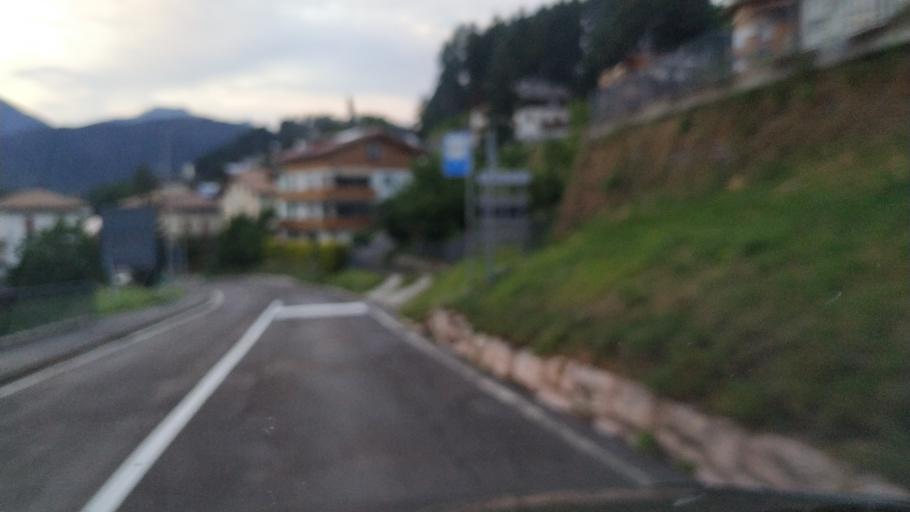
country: IT
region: Trentino-Alto Adige
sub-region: Provincia di Trento
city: Fondo
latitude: 46.4399
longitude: 11.1328
